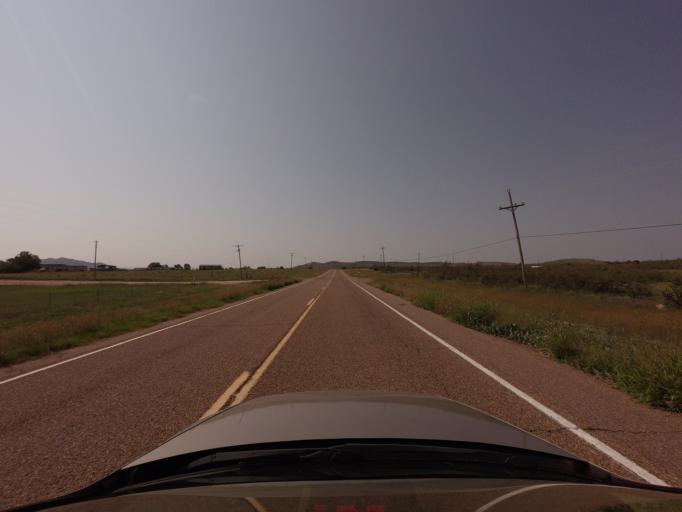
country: US
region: New Mexico
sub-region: Quay County
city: Tucumcari
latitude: 35.1290
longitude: -103.7275
